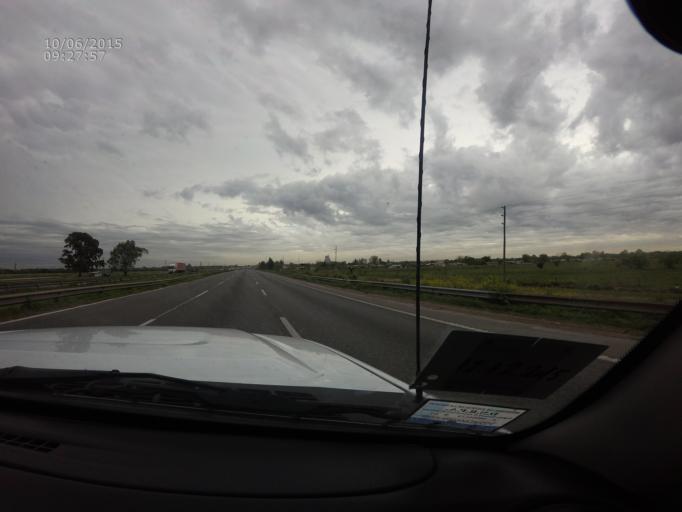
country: AR
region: Buenos Aires
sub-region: Partido de Campana
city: Campana
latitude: -34.1637
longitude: -59.0035
